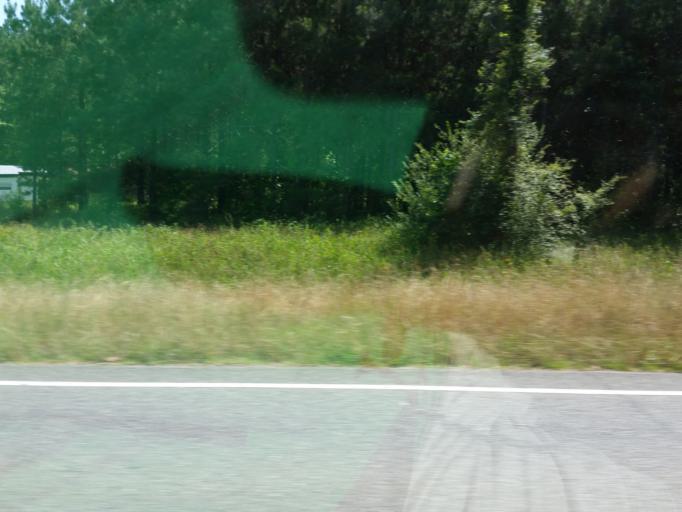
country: US
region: Alabama
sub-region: Marengo County
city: Demopolis
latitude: 32.6439
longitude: -87.8722
